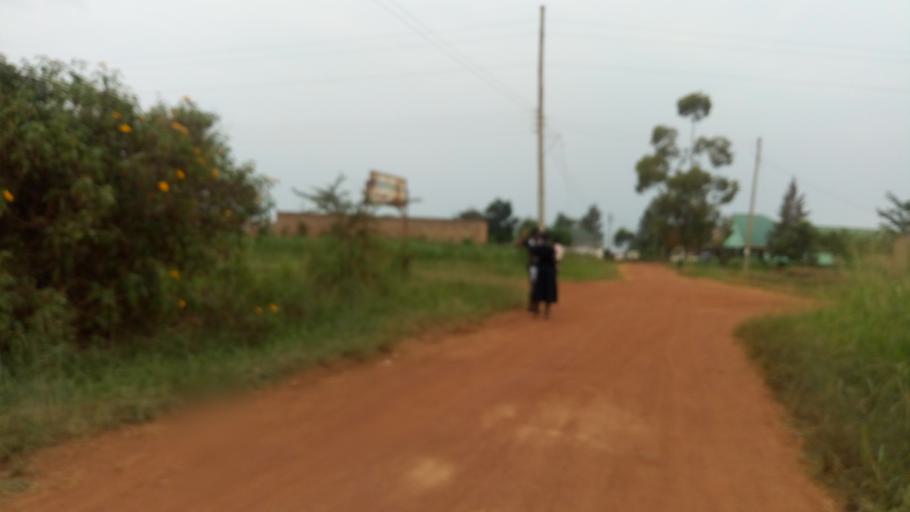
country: UG
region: Western Region
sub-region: Kiryandongo District
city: Kiryandongo
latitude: 1.8037
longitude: 32.0105
